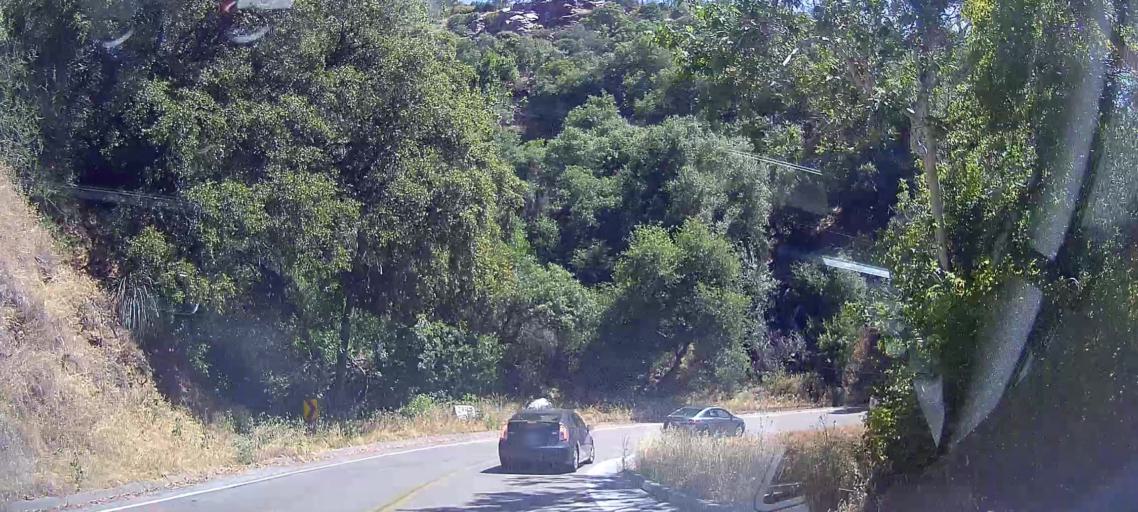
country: US
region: California
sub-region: Tulare County
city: Three Rivers
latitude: 36.5203
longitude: -118.7788
